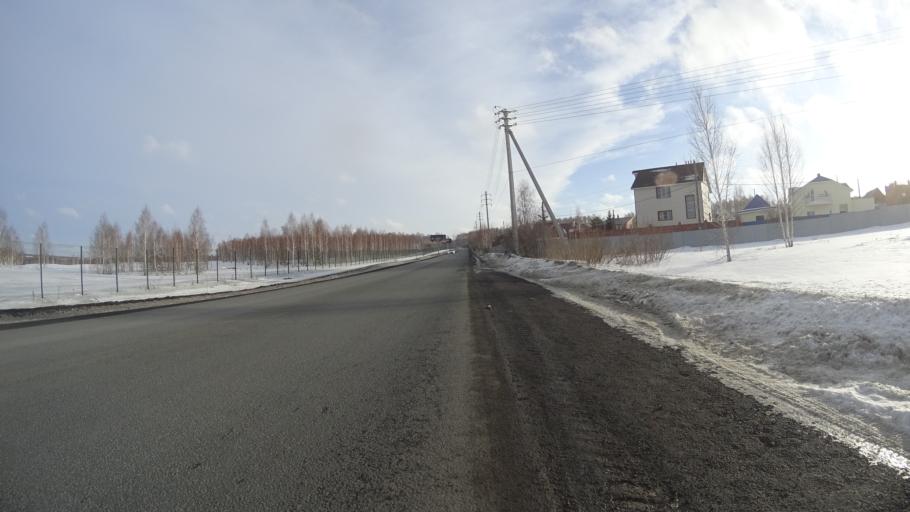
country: RU
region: Chelyabinsk
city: Sargazy
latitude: 55.1329
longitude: 61.2864
